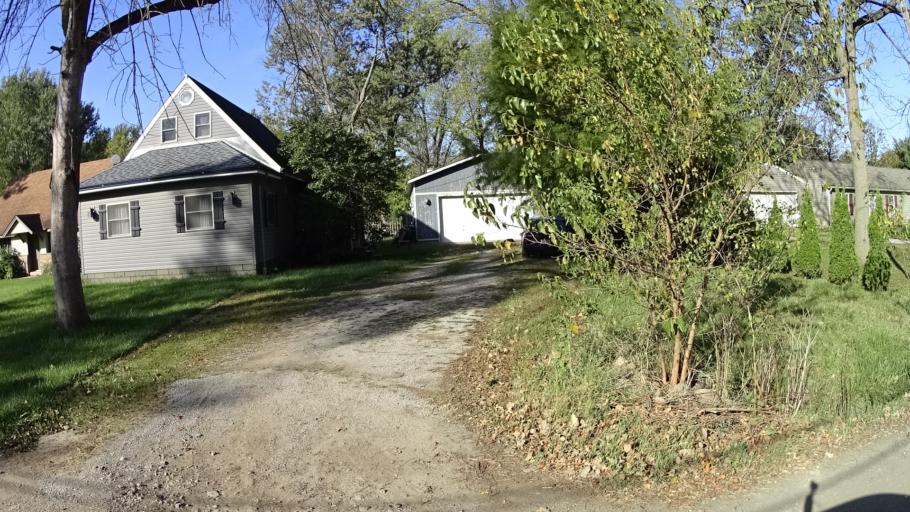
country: US
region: Ohio
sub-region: Lorain County
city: Vermilion-on-the-Lake
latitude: 41.4255
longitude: -82.2915
